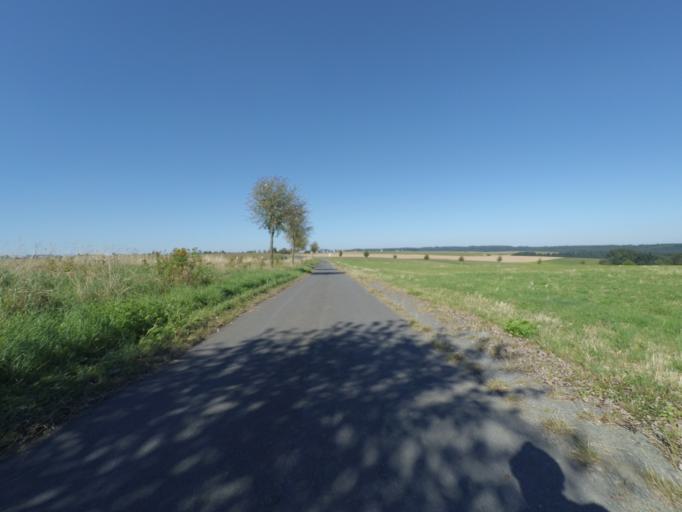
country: DE
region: Rheinland-Pfalz
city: Lutzerath
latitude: 50.1152
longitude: 7.0120
